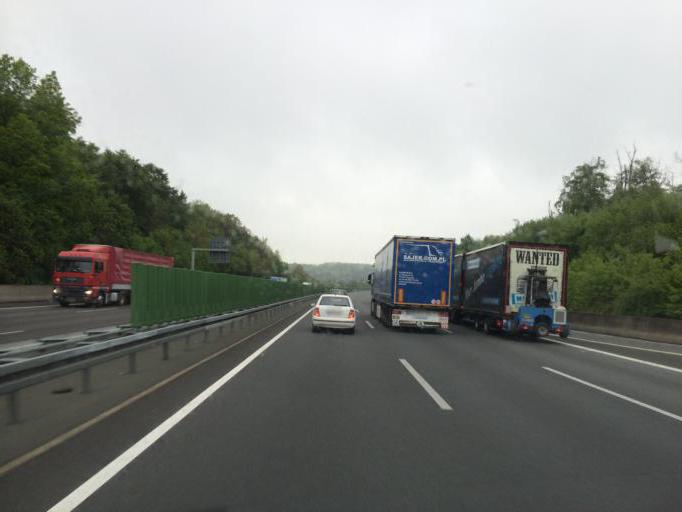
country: DE
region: Lower Saxony
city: Pohle
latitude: 52.2630
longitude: 9.3141
